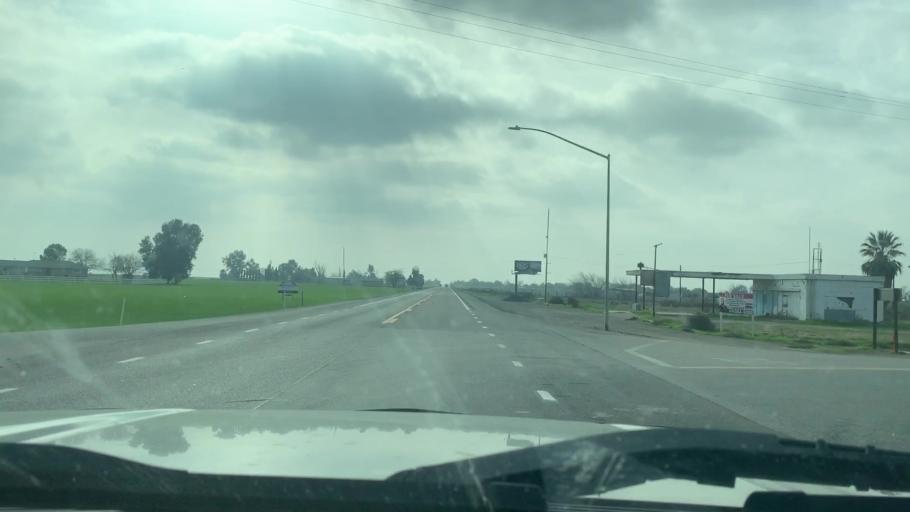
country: US
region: California
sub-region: Kings County
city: Stratford
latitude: 36.1894
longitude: -119.8279
